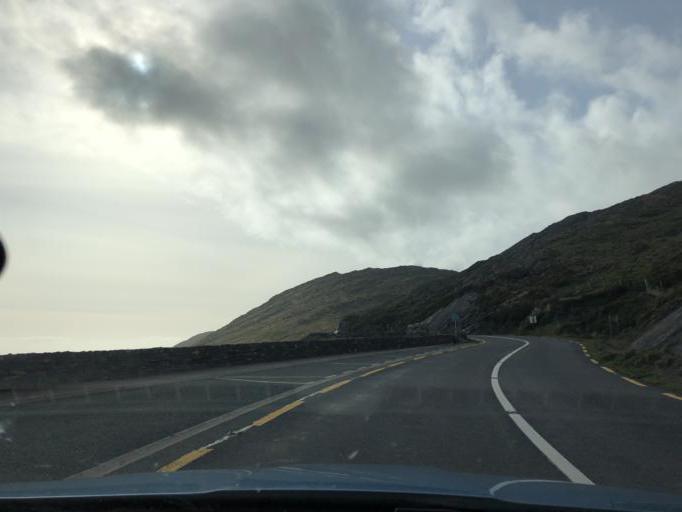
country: IE
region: Munster
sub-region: Ciarrai
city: Cahersiveen
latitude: 51.7746
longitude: -10.1600
